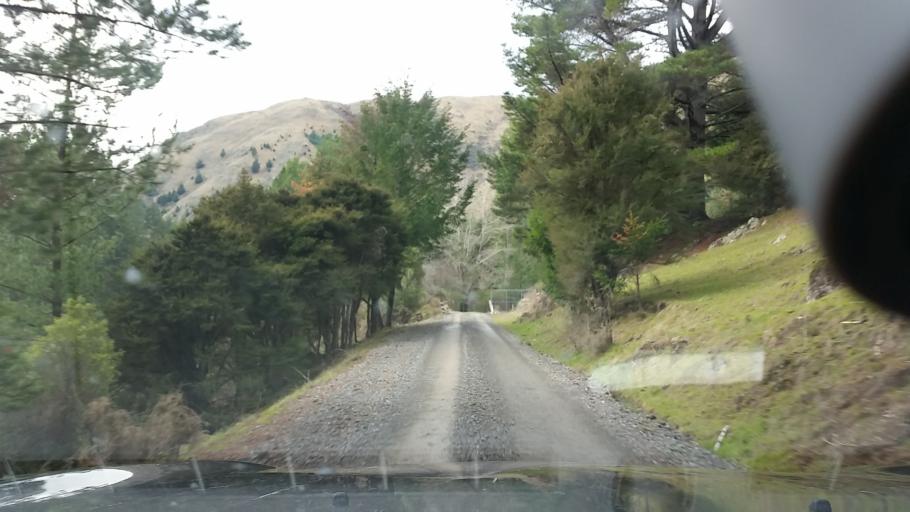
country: NZ
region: Tasman
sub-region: Tasman District
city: Richmond
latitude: -41.7302
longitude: 173.4671
